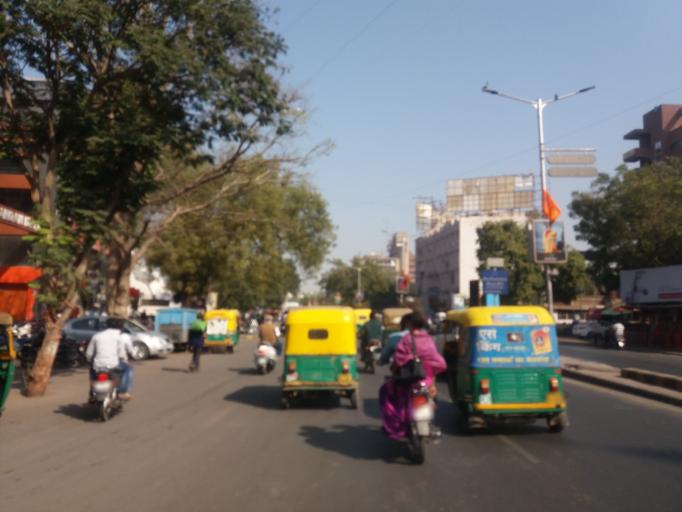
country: IN
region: Gujarat
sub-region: Ahmadabad
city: Ahmedabad
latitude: 23.0238
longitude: 72.5712
